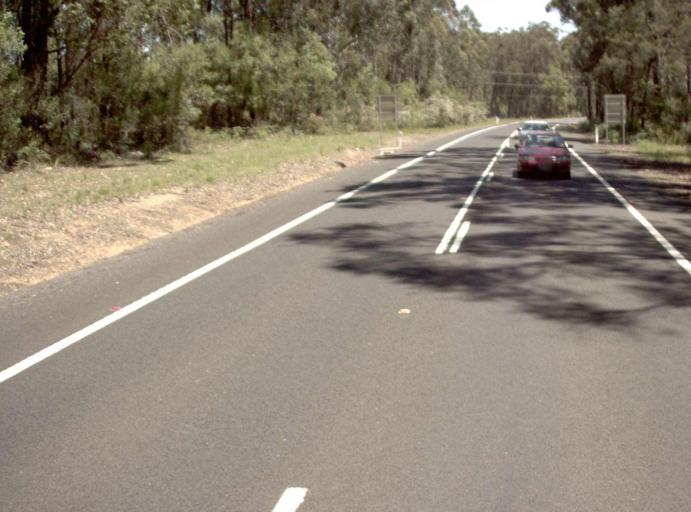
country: AU
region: Victoria
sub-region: East Gippsland
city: Lakes Entrance
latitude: -37.6984
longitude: 148.5879
